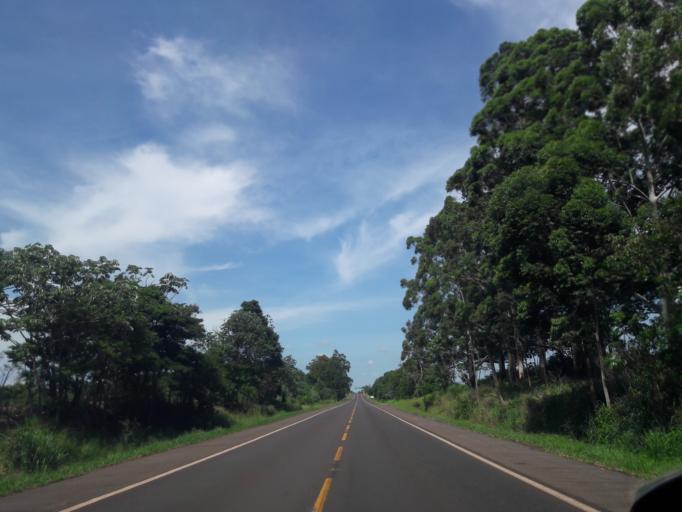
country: BR
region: Parana
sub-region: Campo Mourao
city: Campo Mourao
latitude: -24.2789
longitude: -52.5297
